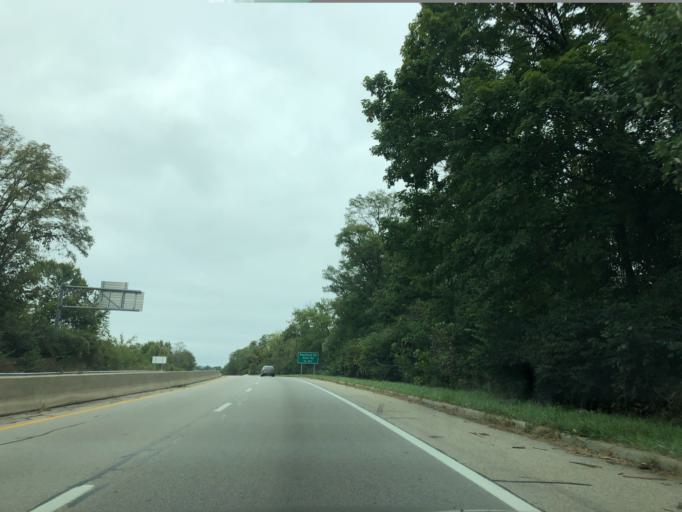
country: US
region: Ohio
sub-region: Hamilton County
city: Dillonvale
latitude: 39.2220
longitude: -84.4082
